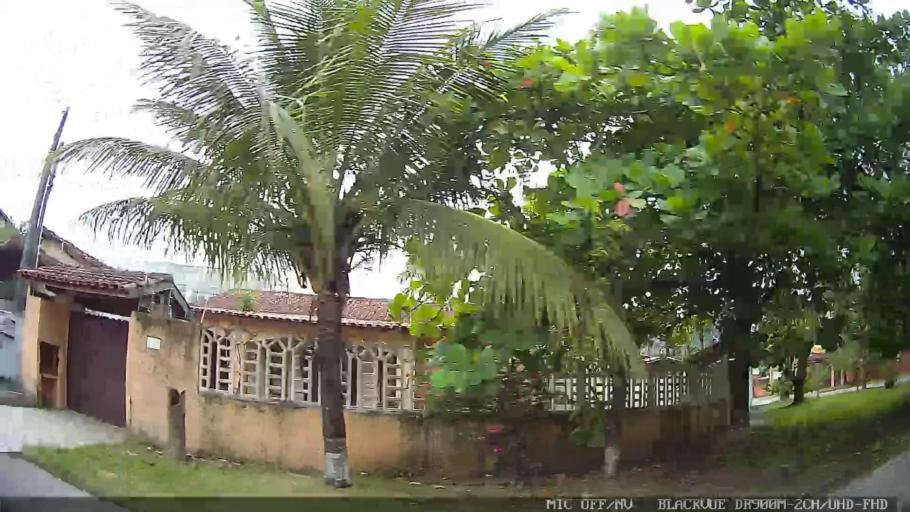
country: BR
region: Sao Paulo
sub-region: Caraguatatuba
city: Caraguatatuba
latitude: -23.6423
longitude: -45.4301
